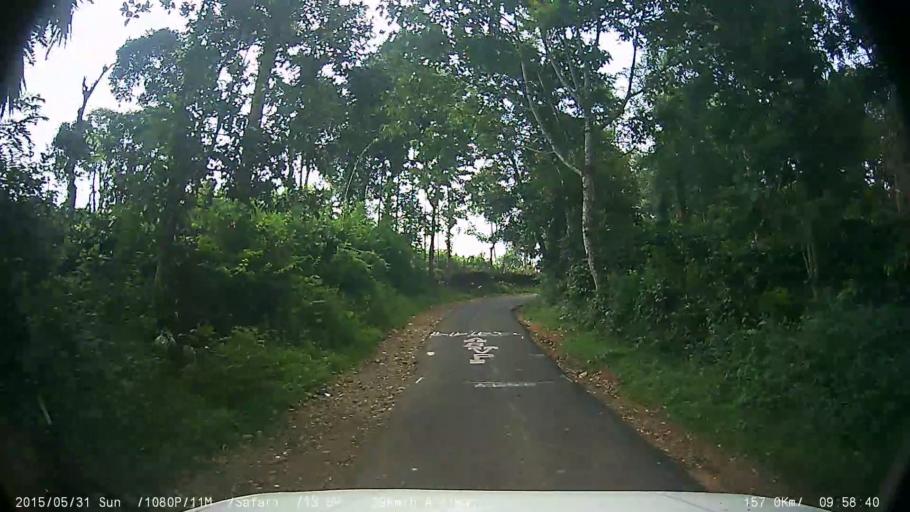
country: IN
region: Kerala
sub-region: Wayanad
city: Kalpetta
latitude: 11.5918
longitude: 76.0645
